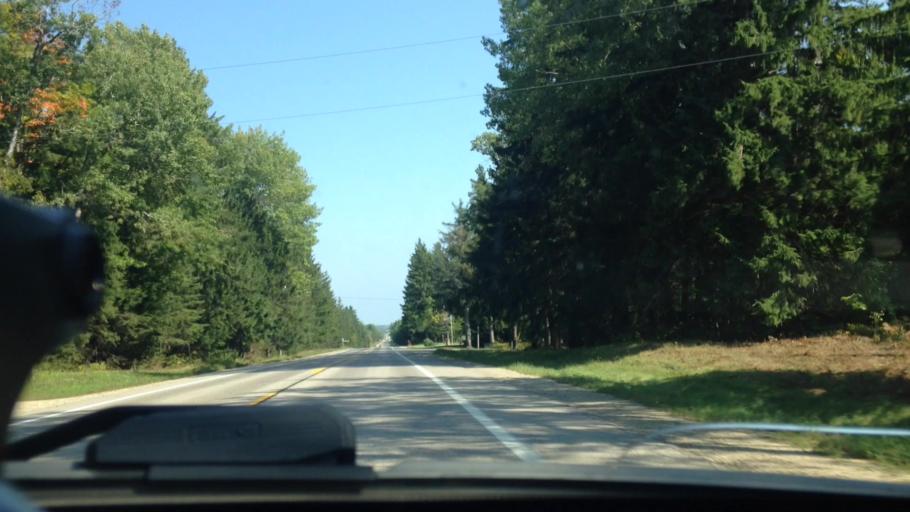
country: US
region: Michigan
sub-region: Luce County
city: Newberry
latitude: 46.3037
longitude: -85.4381
